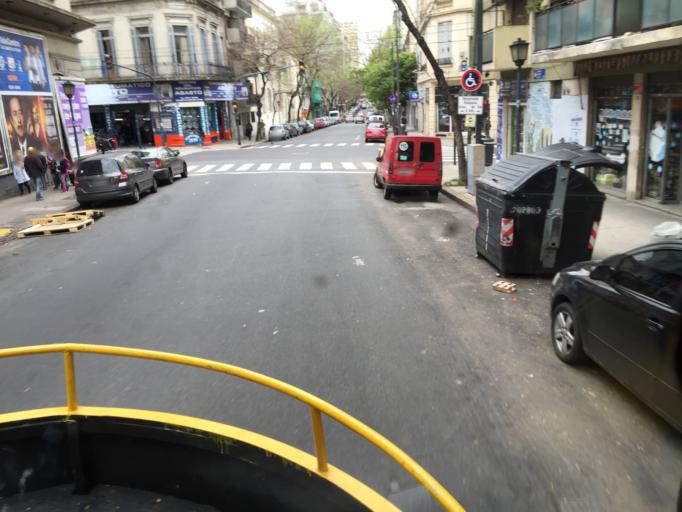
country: AR
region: Buenos Aires F.D.
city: Buenos Aires
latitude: -34.6051
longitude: -58.4111
